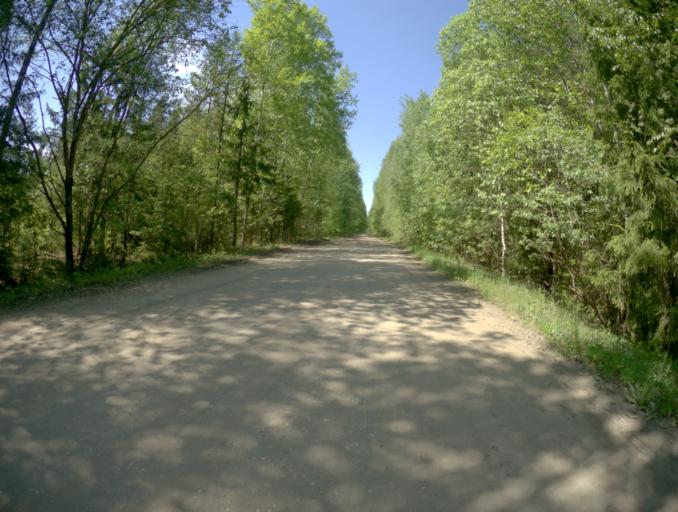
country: RU
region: Vladimir
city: Gusevskiy
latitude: 55.6949
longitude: 40.5593
